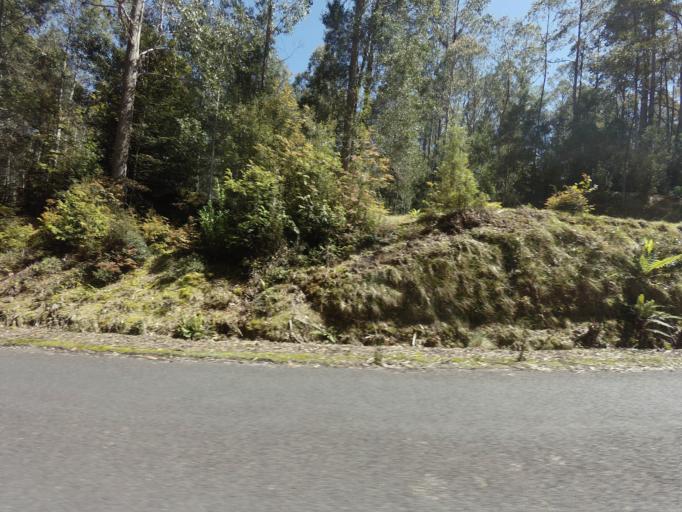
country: AU
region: Tasmania
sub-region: Huon Valley
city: Geeveston
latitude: -42.8175
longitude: 146.3449
